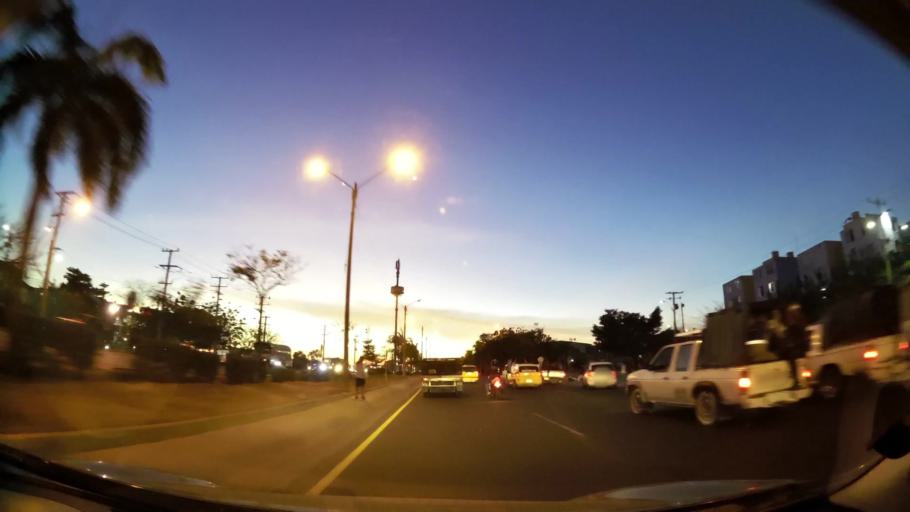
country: CO
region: Atlantico
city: Soledad
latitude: 10.9228
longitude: -74.8114
